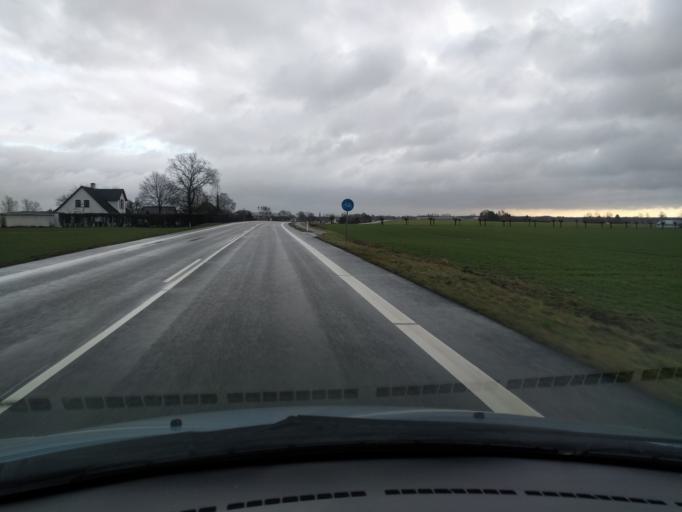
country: DK
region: South Denmark
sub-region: Kerteminde Kommune
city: Langeskov
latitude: 55.3827
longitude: 10.5379
